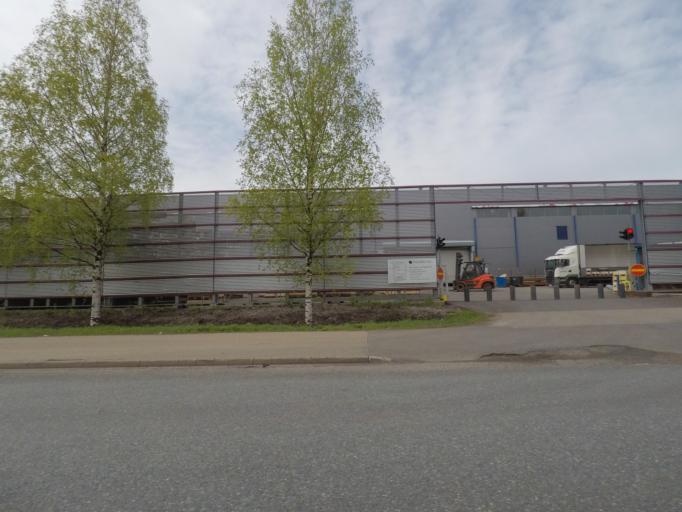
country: FI
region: Uusimaa
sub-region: Helsinki
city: Vantaa
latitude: 60.2955
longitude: 24.9958
